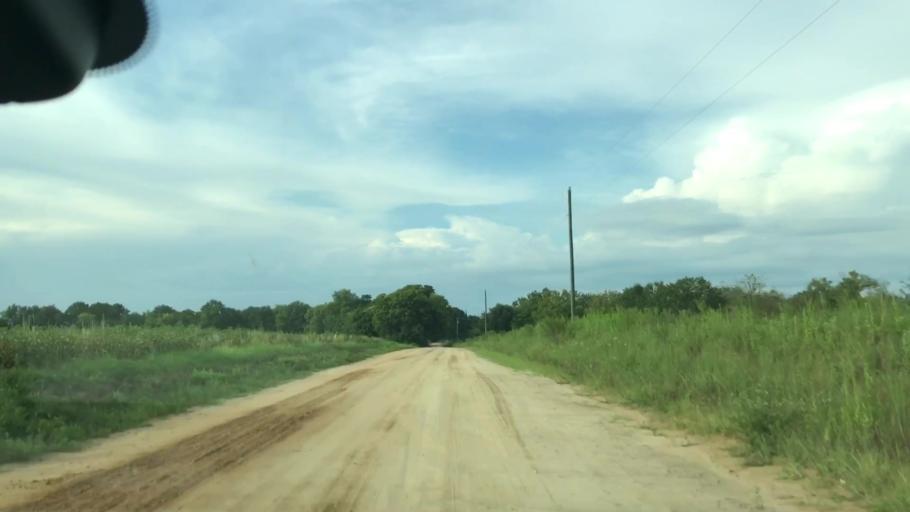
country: US
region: Georgia
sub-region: Clay County
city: Fort Gaines
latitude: 31.7192
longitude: -85.0668
